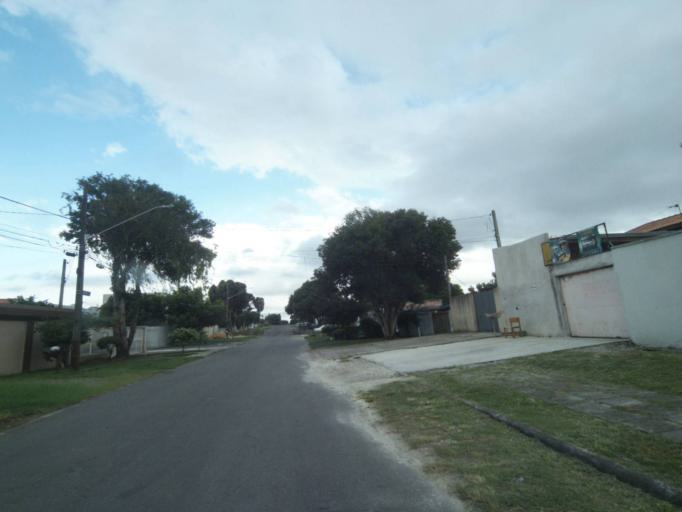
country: BR
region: Parana
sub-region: Pinhais
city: Pinhais
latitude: -25.4449
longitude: -49.2113
